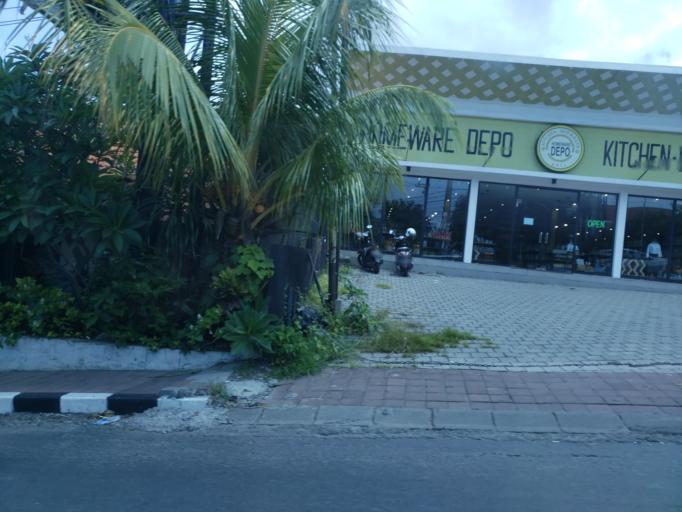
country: ID
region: Bali
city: Jimbaran
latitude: -8.8083
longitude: 115.1583
